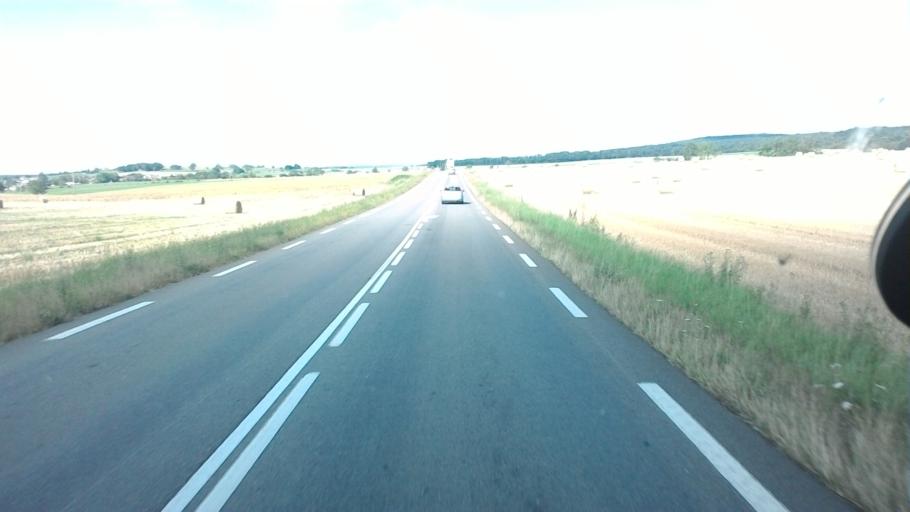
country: FR
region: Franche-Comte
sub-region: Departement de la Haute-Saone
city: Gy
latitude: 47.4486
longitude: 5.8898
